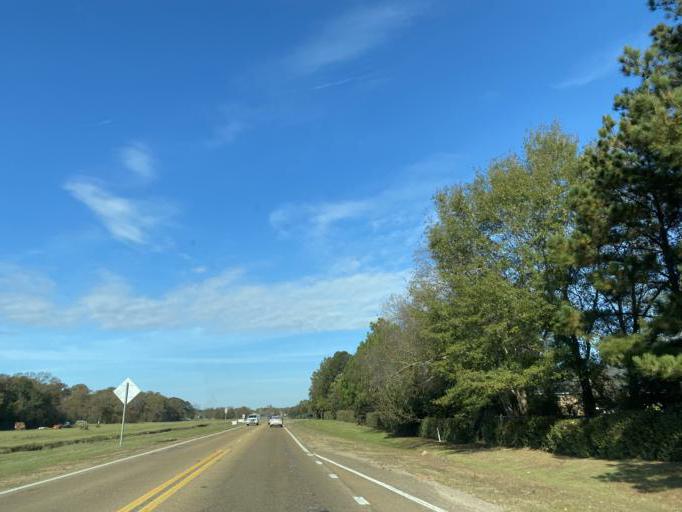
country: US
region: Mississippi
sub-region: Madison County
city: Madison
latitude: 32.4752
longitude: -90.1517
